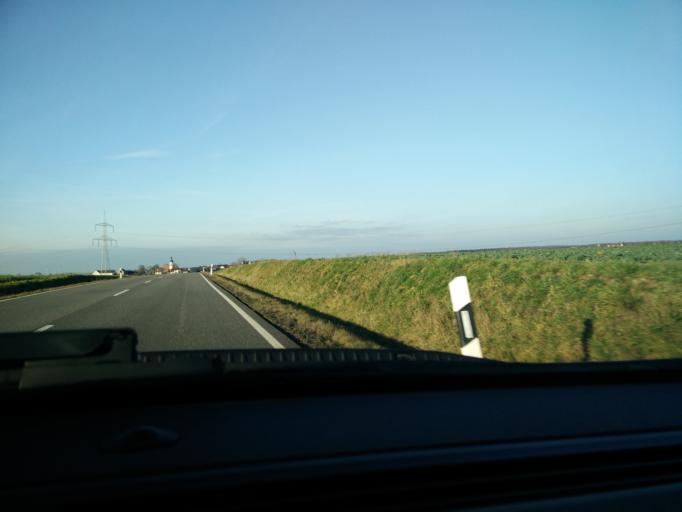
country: DE
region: Saxony
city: Geithain
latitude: 51.0921
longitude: 12.7055
